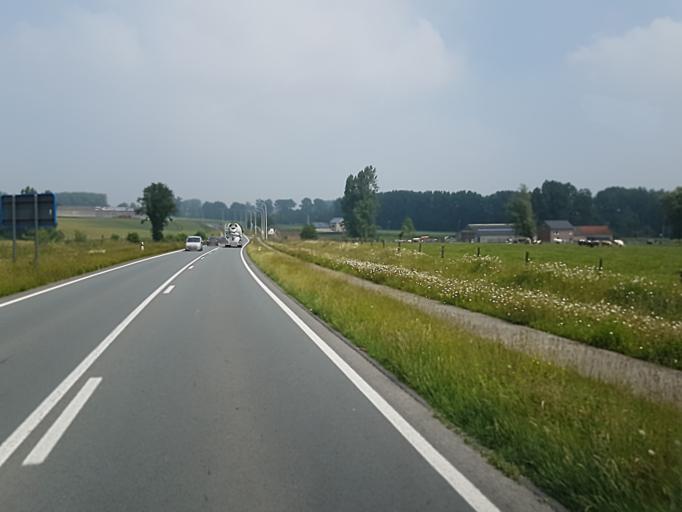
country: BE
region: Flanders
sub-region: Provincie Oost-Vlaanderen
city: Sint-Maria-Lierde
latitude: 50.8380
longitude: 3.8678
